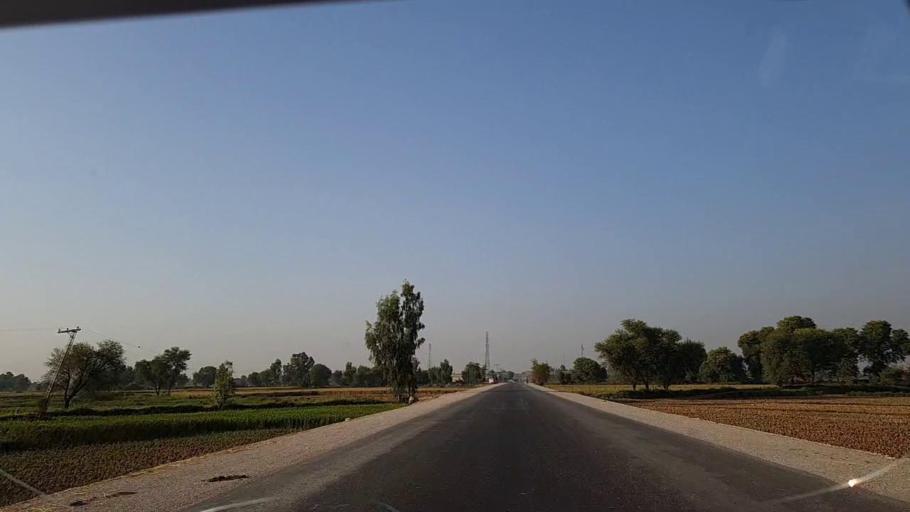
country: PK
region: Sindh
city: Rustam jo Goth
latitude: 27.9578
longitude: 68.8073
